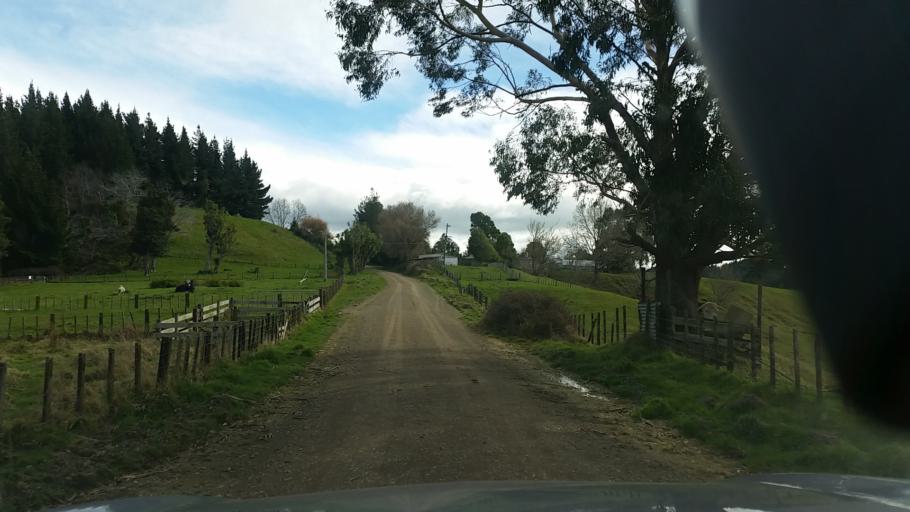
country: NZ
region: Hawke's Bay
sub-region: Napier City
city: Napier
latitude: -39.2296
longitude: 176.9894
